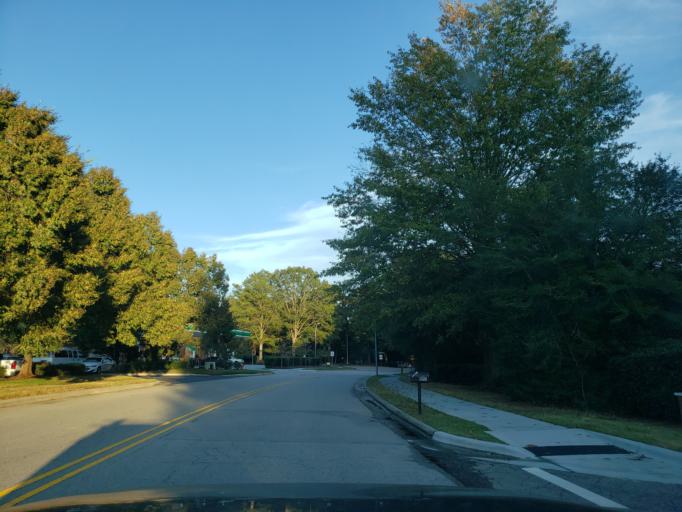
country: US
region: North Carolina
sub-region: Wake County
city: Apex
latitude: 35.7398
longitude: -78.8064
